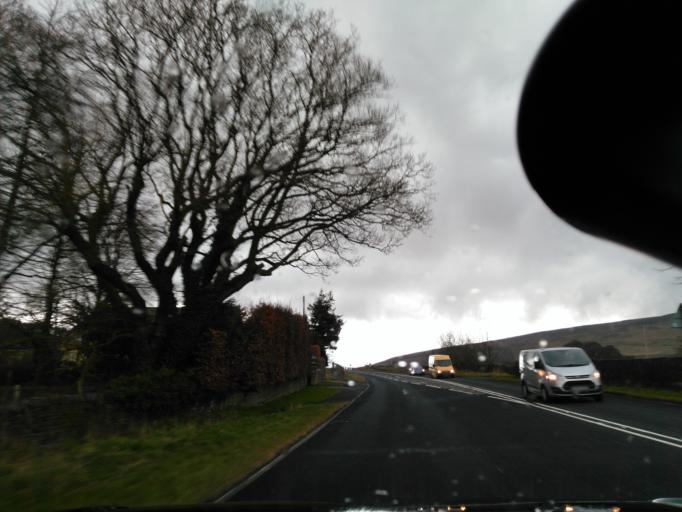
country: GB
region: England
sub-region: Bradford
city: Addingham
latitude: 53.9741
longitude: -1.8717
